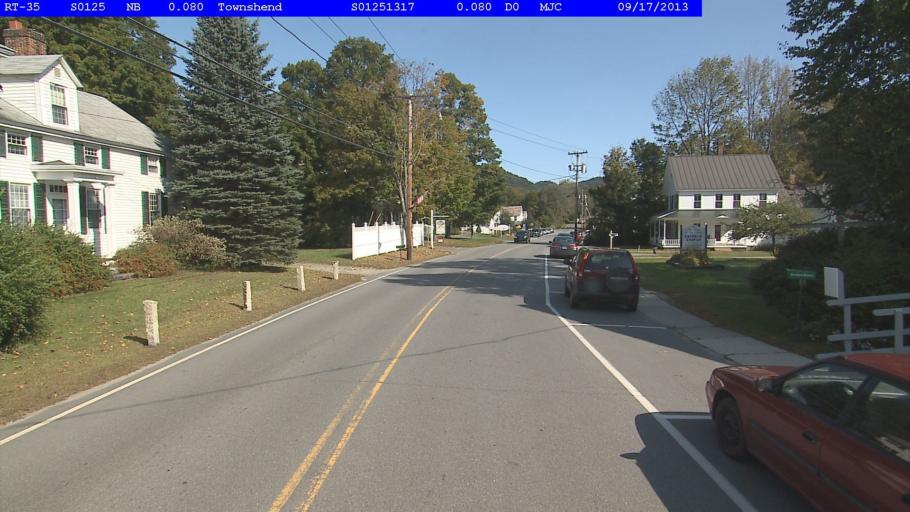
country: US
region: Vermont
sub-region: Windham County
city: Newfane
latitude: 43.0472
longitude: -72.6681
